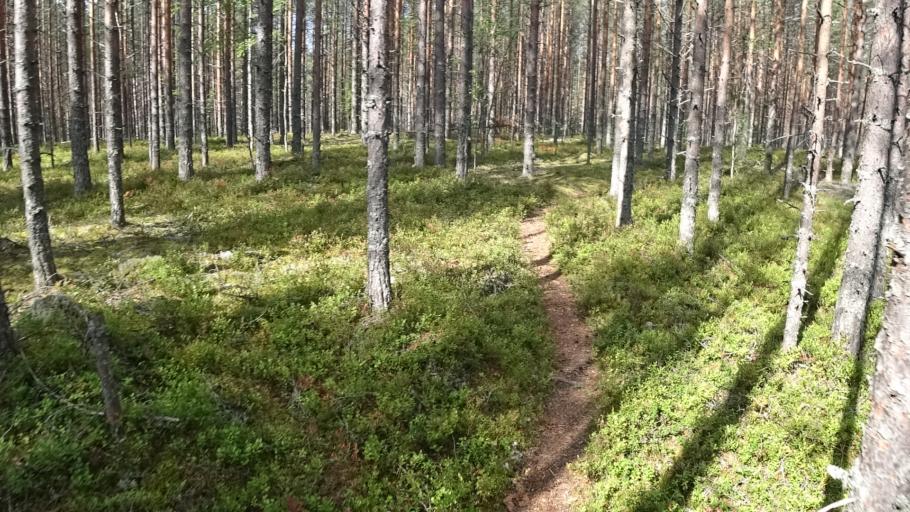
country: FI
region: North Karelia
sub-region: Joensuu
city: Ilomantsi
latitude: 62.6055
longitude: 31.1885
